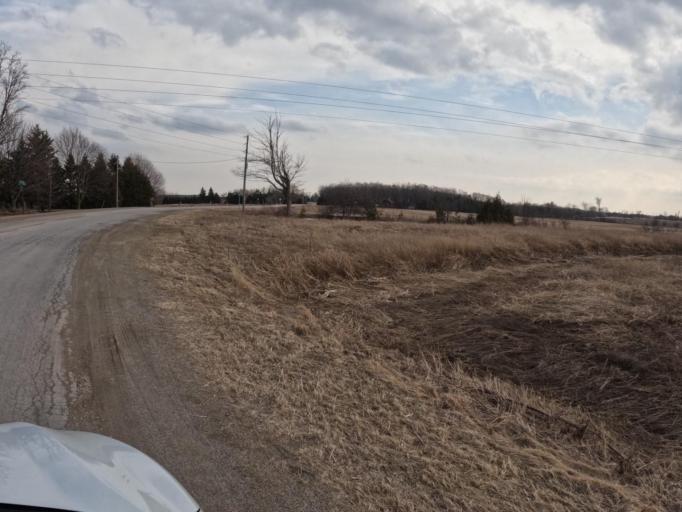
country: CA
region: Ontario
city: Shelburne
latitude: 43.9267
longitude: -80.3078
